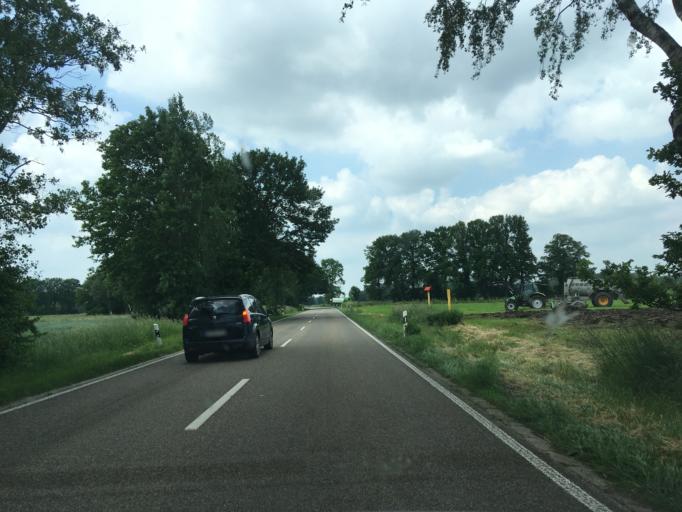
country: DE
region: North Rhine-Westphalia
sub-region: Regierungsbezirk Munster
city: Raesfeld
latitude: 51.7709
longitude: 6.8134
